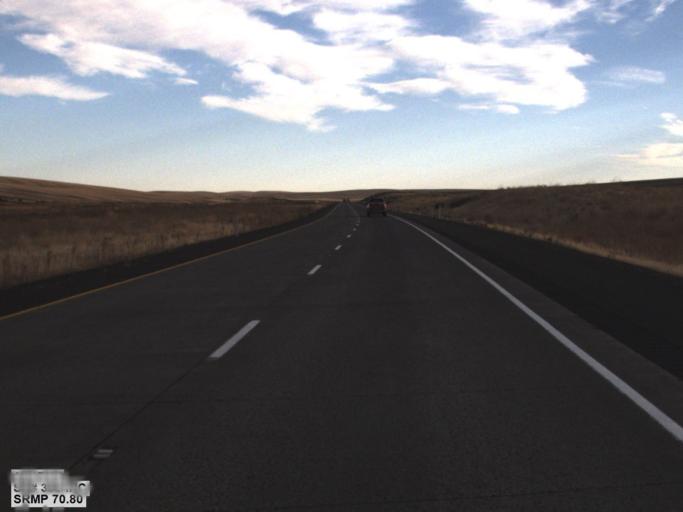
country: US
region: Washington
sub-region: Franklin County
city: Connell
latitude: 46.8244
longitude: -118.6706
